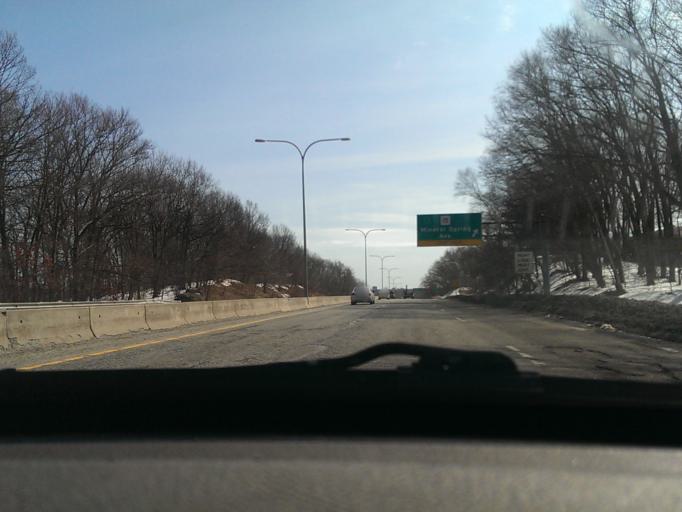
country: US
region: Rhode Island
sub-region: Providence County
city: North Providence
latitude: 41.8719
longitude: -71.4313
